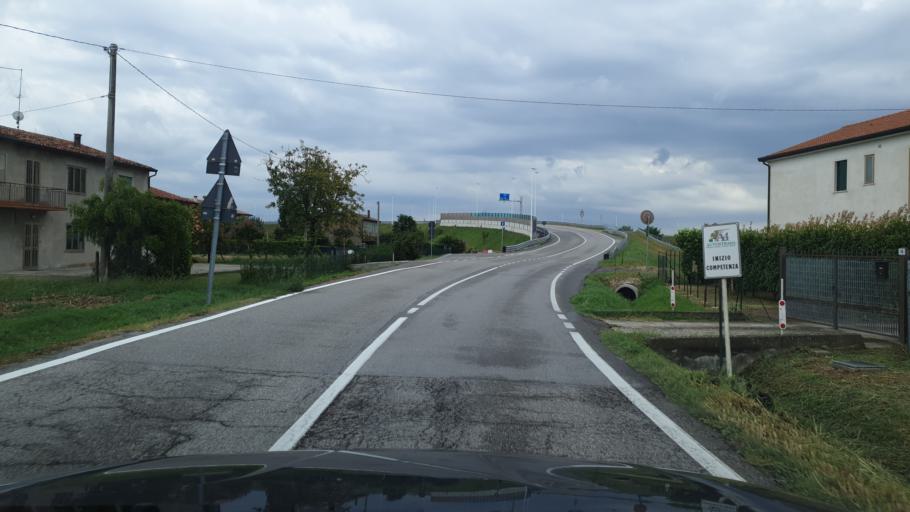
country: IT
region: Veneto
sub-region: Provincia di Vicenza
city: Noventa Vicentina
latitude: 45.2745
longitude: 11.5673
